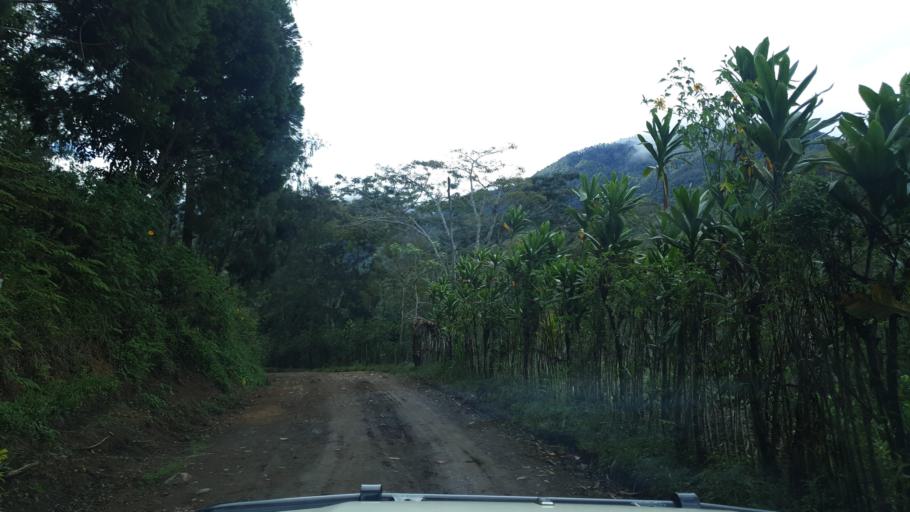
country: PG
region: Eastern Highlands
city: Goroka
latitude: -5.9229
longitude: 145.2640
